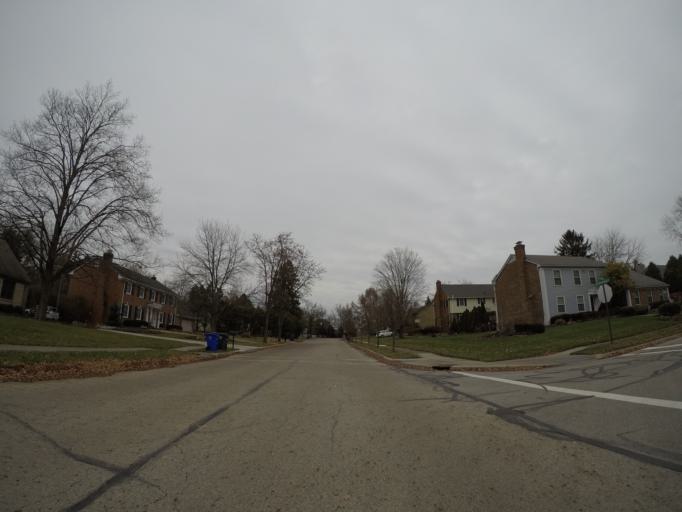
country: US
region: Ohio
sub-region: Franklin County
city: Dublin
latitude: 40.0508
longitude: -83.0858
